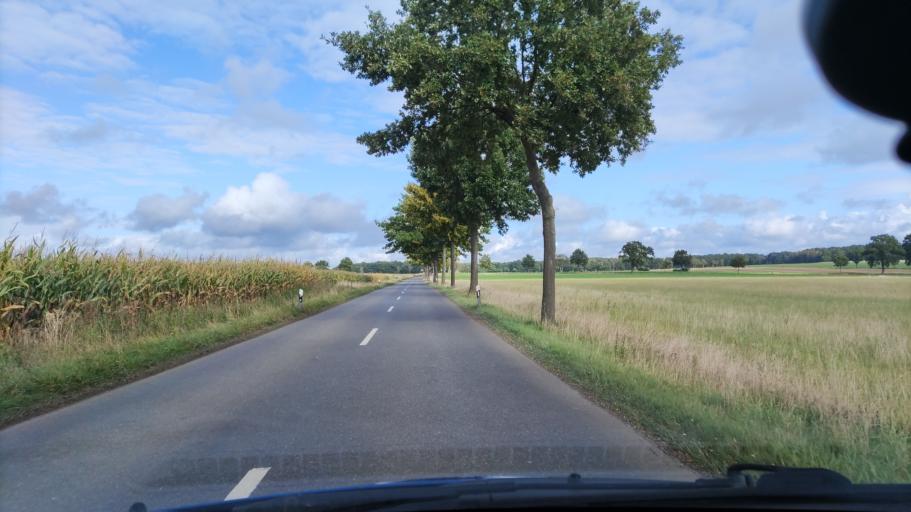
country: DE
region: Lower Saxony
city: Romstedt
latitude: 53.0829
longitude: 10.6710
